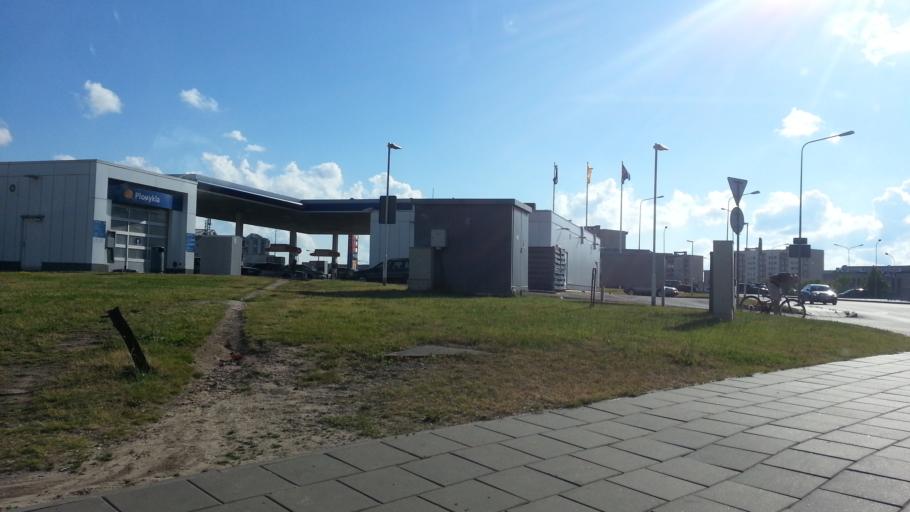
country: LT
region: Vilnius County
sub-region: Vilnius
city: Fabijoniskes
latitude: 54.7308
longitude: 25.2396
